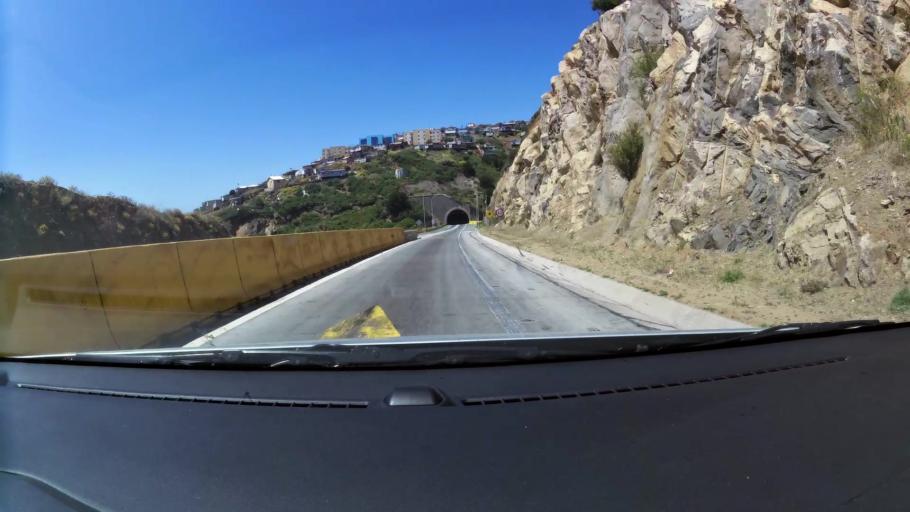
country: CL
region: Valparaiso
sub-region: Provincia de Valparaiso
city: Valparaiso
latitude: -33.0473
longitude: -71.6567
